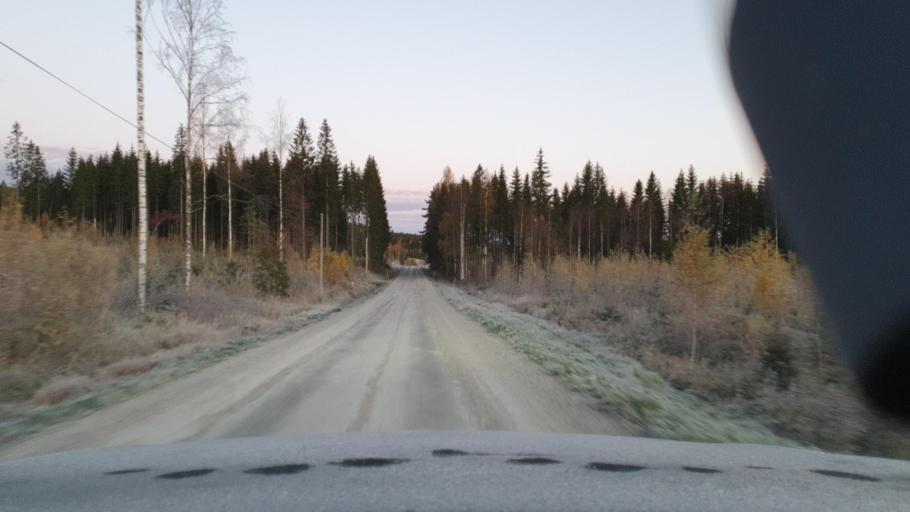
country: SE
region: Vaermland
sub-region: Arvika Kommun
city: Arvika
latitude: 59.7909
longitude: 12.7568
